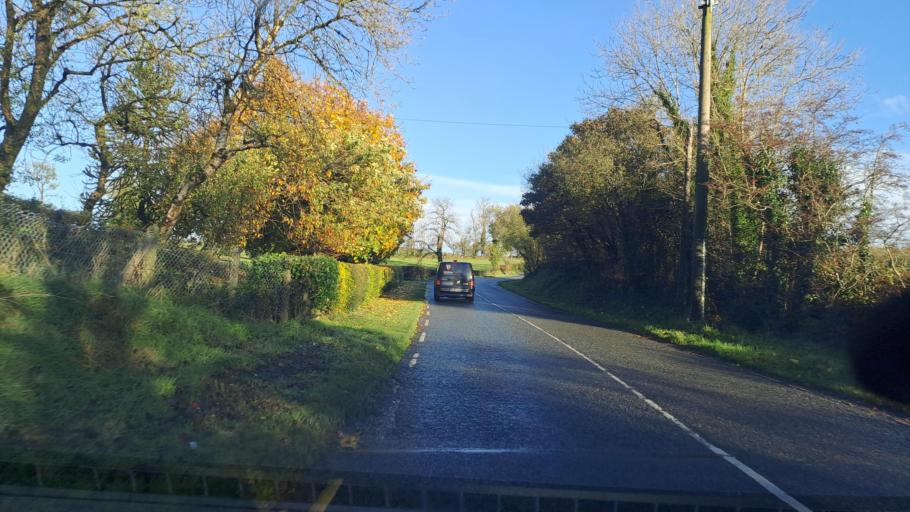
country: IE
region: Ulster
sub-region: County Monaghan
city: Monaghan
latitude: 54.1792
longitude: -6.9957
